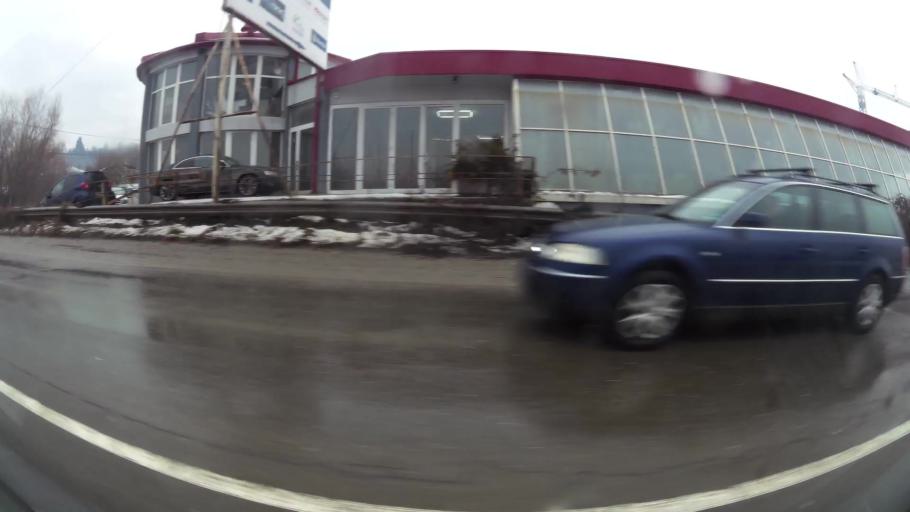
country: BG
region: Sofiya
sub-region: Obshtina Bozhurishte
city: Bozhurishte
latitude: 42.6892
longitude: 23.2306
